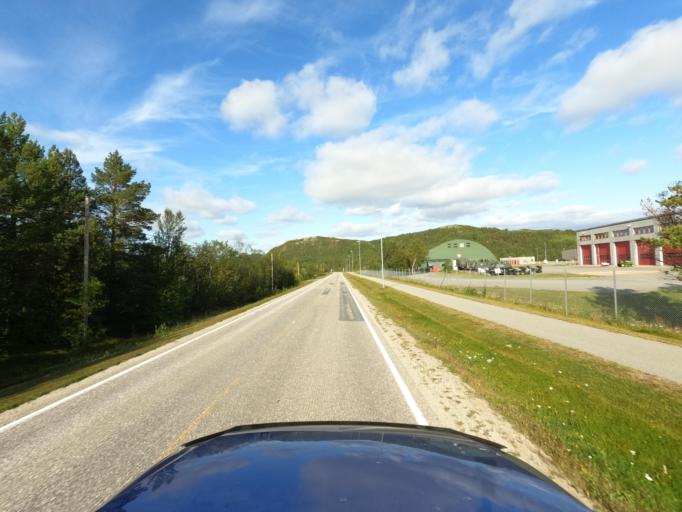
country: NO
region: Finnmark Fylke
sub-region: Porsanger
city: Lakselv
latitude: 69.9056
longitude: 24.9981
